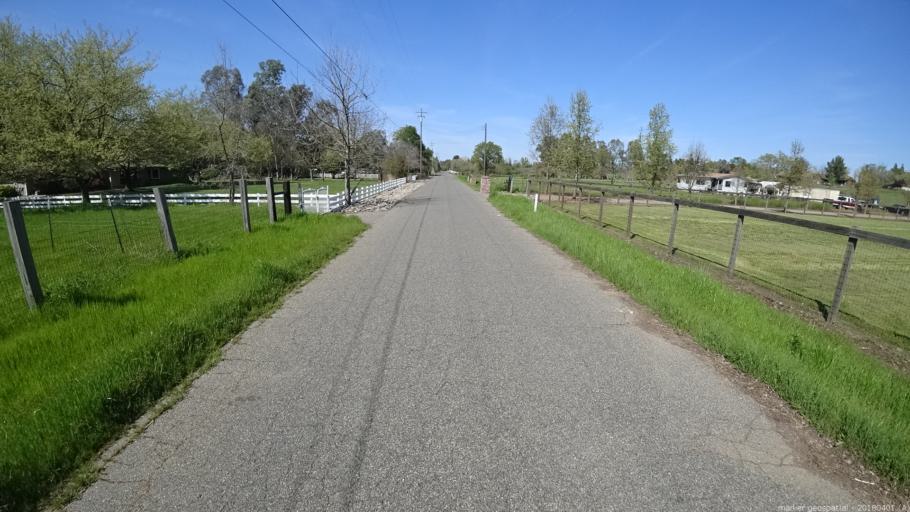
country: US
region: California
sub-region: Sacramento County
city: Wilton
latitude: 38.4080
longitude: -121.2521
